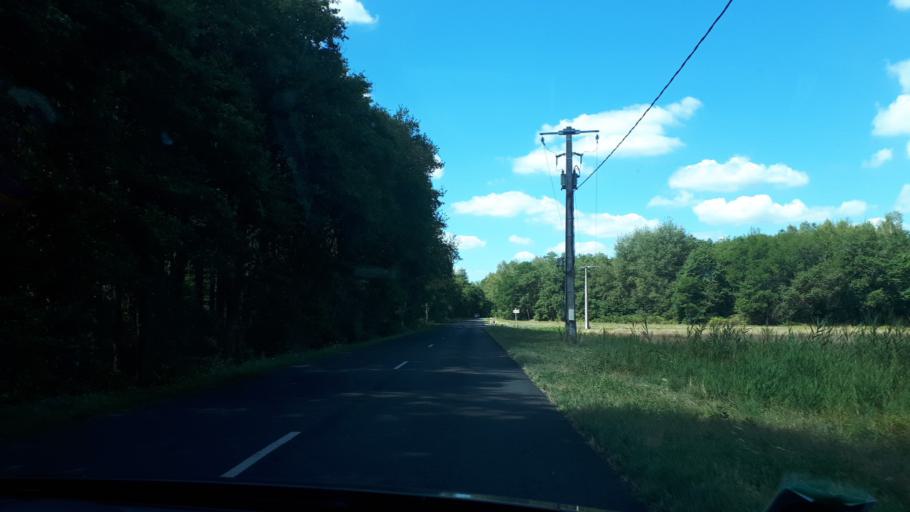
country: FR
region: Centre
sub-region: Departement du Loir-et-Cher
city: Neung-sur-Beuvron
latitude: 47.5341
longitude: 1.7506
